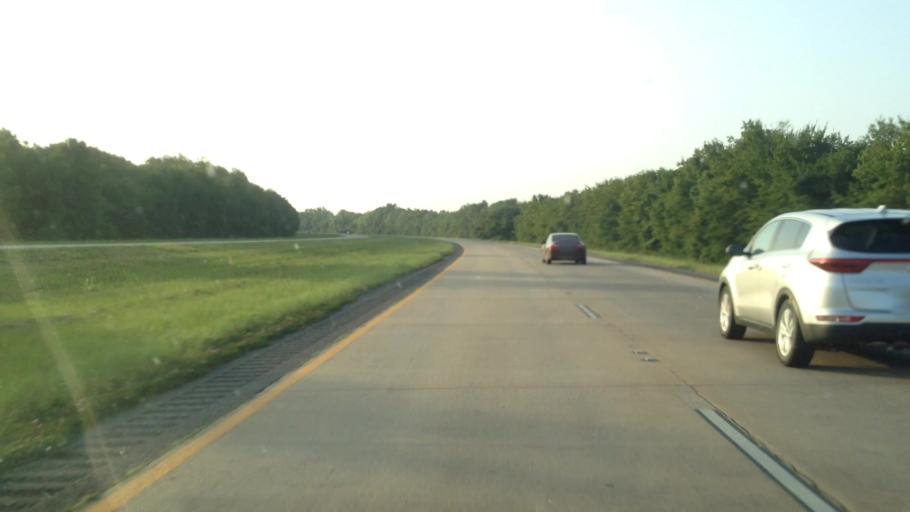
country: US
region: Louisiana
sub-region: Natchitoches Parish
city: Vienna Bend
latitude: 31.5738
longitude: -93.0177
